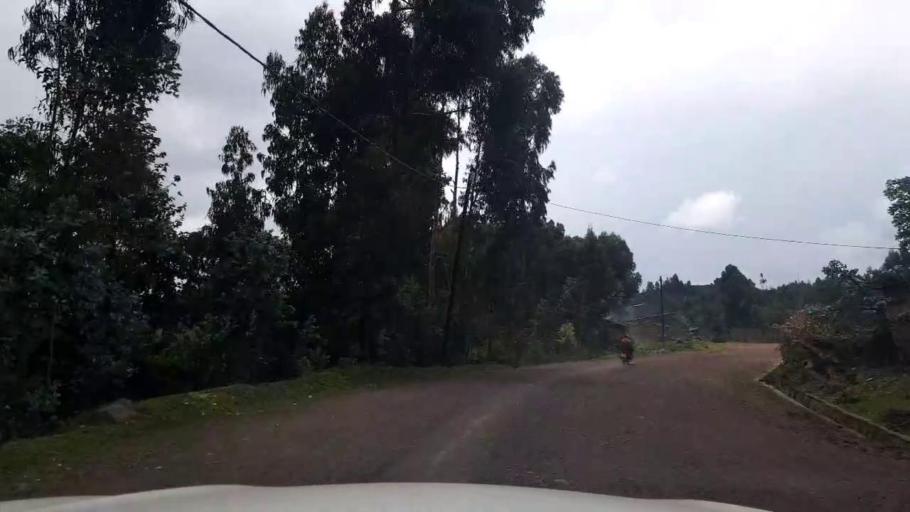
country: RW
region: Northern Province
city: Musanze
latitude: -1.5782
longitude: 29.4855
